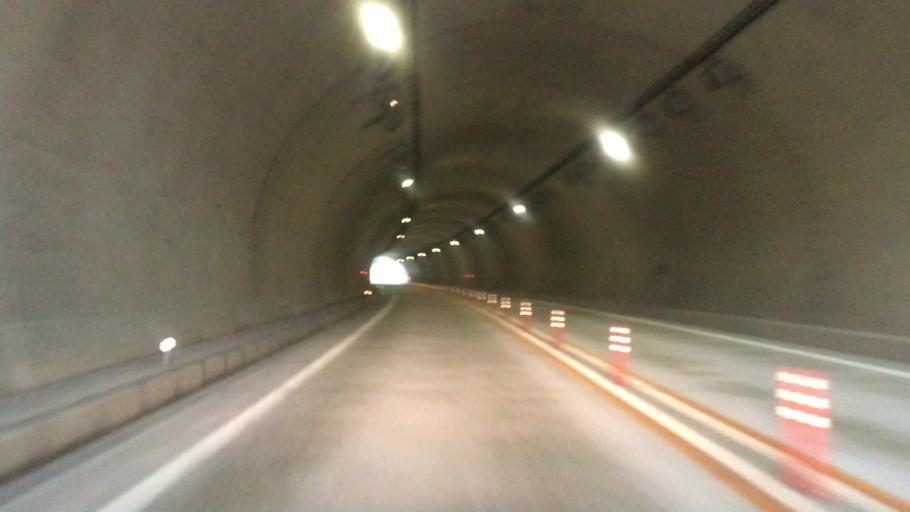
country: JP
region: Tottori
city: Tottori
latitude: 35.5552
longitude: 134.2810
